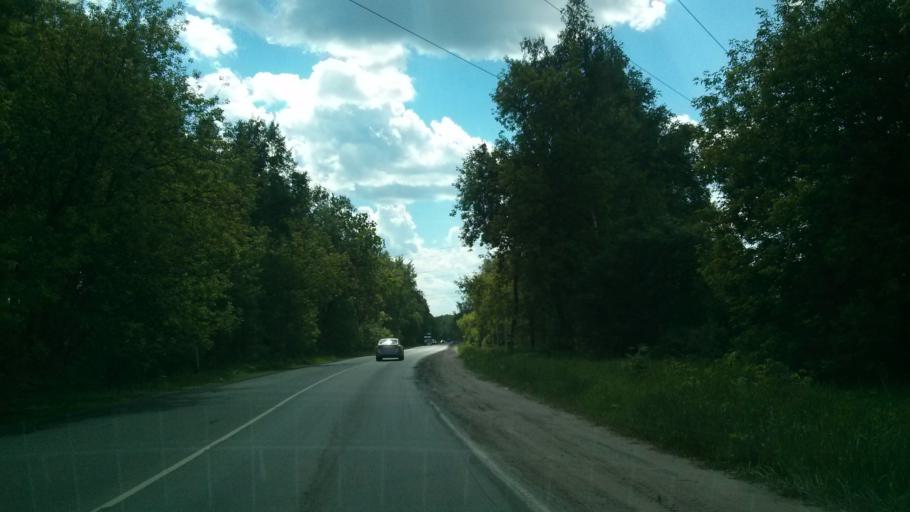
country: RU
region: Vladimir
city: Murom
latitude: 55.5488
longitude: 41.9976
